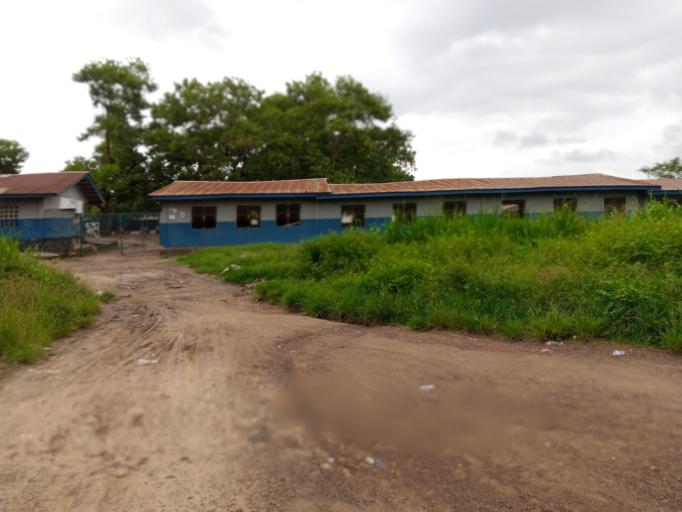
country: SL
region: Eastern Province
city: Kenema
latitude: 7.8610
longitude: -11.1971
